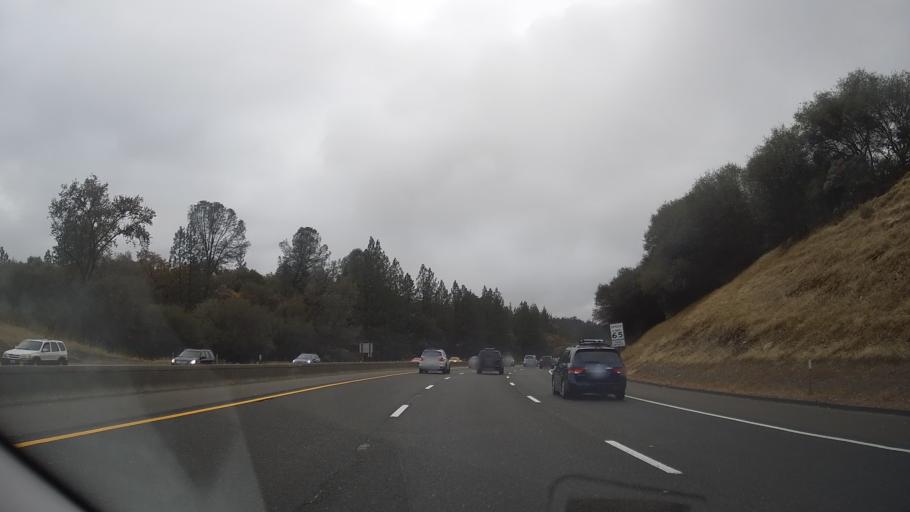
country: US
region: California
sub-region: Placer County
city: Meadow Vista
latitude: 38.9650
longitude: -121.0217
